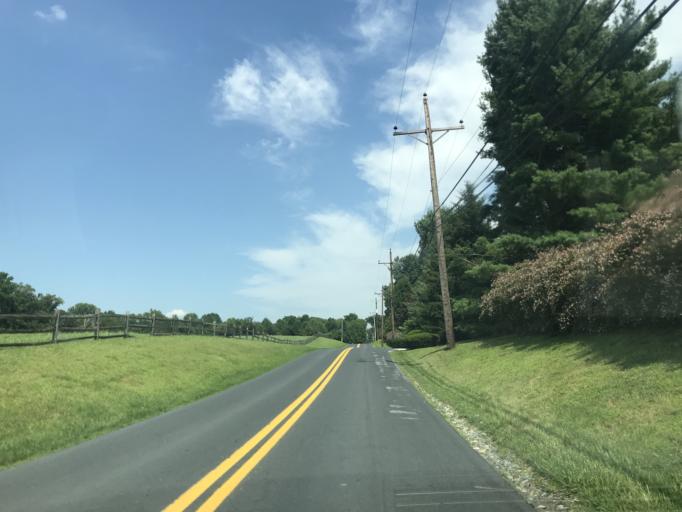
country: US
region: Delaware
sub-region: New Castle County
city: Greenville
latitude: 39.8189
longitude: -75.6108
